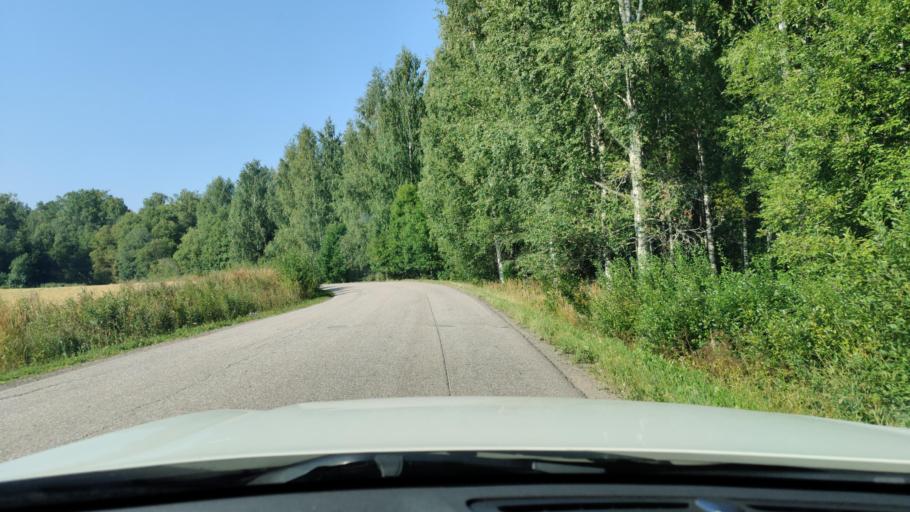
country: FI
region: Haeme
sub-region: Riihimaeki
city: Riihimaeki
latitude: 60.7139
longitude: 24.6942
